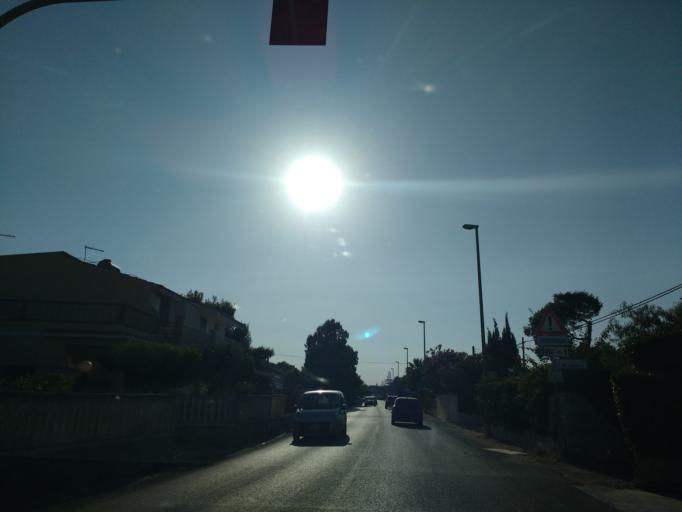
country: IT
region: Sicily
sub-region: Ragusa
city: Ispica
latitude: 36.7278
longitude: 14.9069
